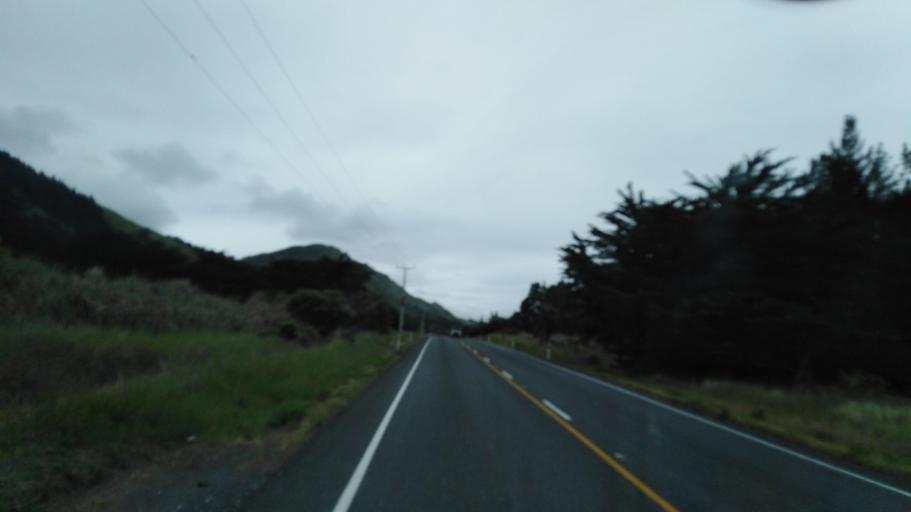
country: NZ
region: Canterbury
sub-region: Kaikoura District
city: Kaikoura
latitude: -42.0637
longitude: 173.9499
